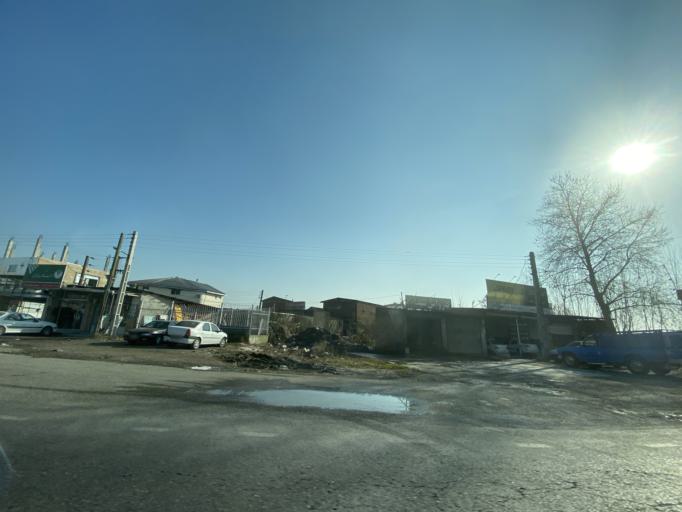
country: IR
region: Mazandaran
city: Babol
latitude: 36.5036
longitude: 52.5322
